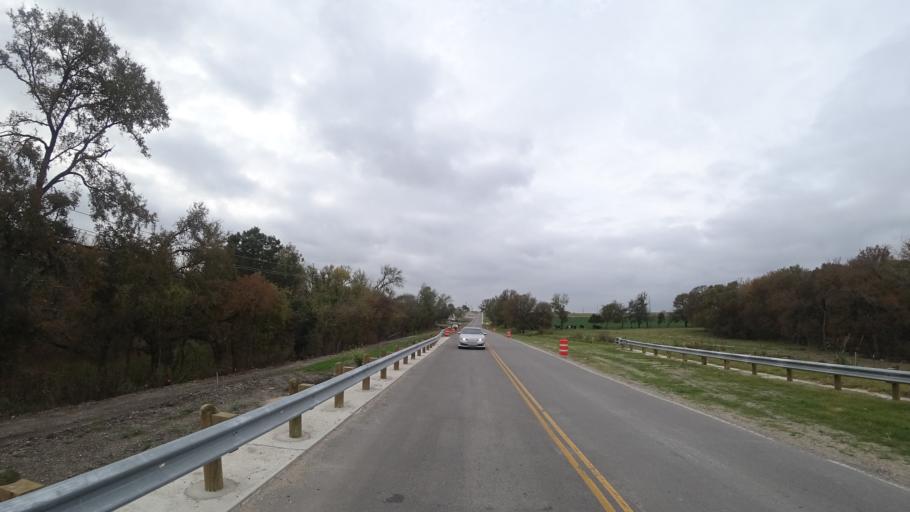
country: US
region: Texas
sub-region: Travis County
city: Pflugerville
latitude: 30.4250
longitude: -97.5758
